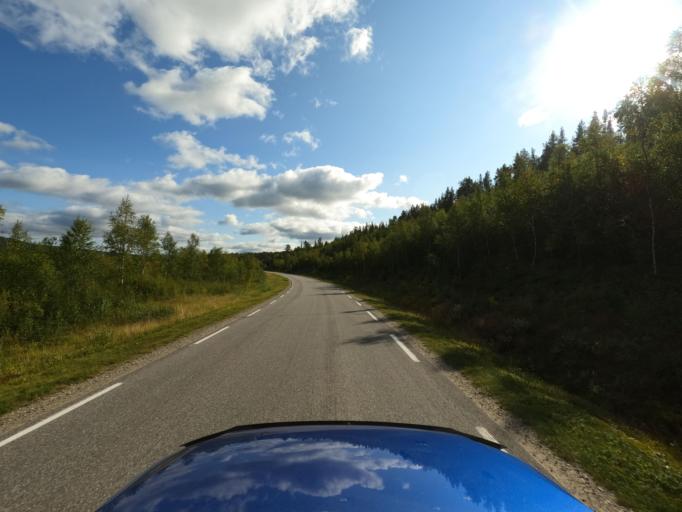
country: NO
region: Finnmark Fylke
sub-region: Karasjok
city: Karasjohka
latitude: 69.4495
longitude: 25.5874
